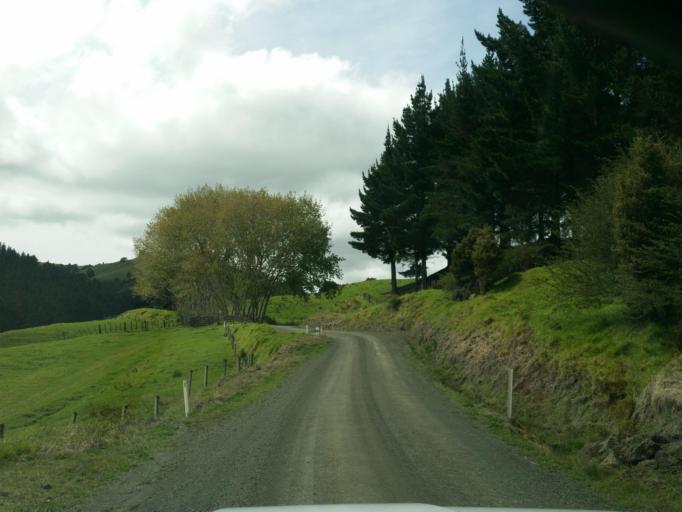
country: NZ
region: Northland
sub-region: Kaipara District
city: Dargaville
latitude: -35.8773
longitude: 174.0518
